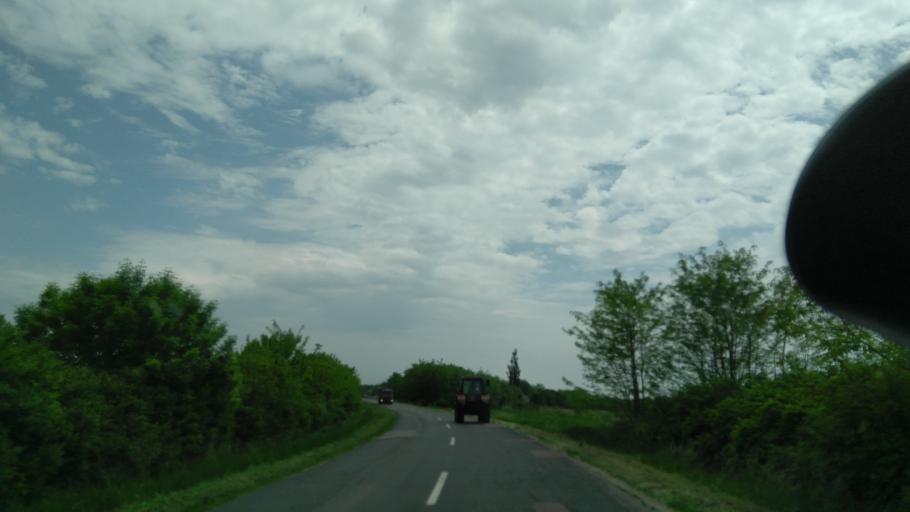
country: HU
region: Hajdu-Bihar
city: Komadi
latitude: 47.0193
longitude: 21.5799
